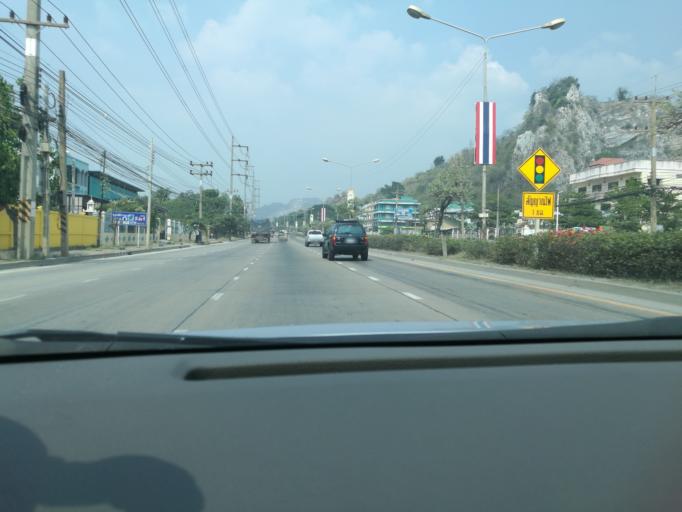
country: TH
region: Sara Buri
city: Phra Phutthabat
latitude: 14.6942
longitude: 100.8672
